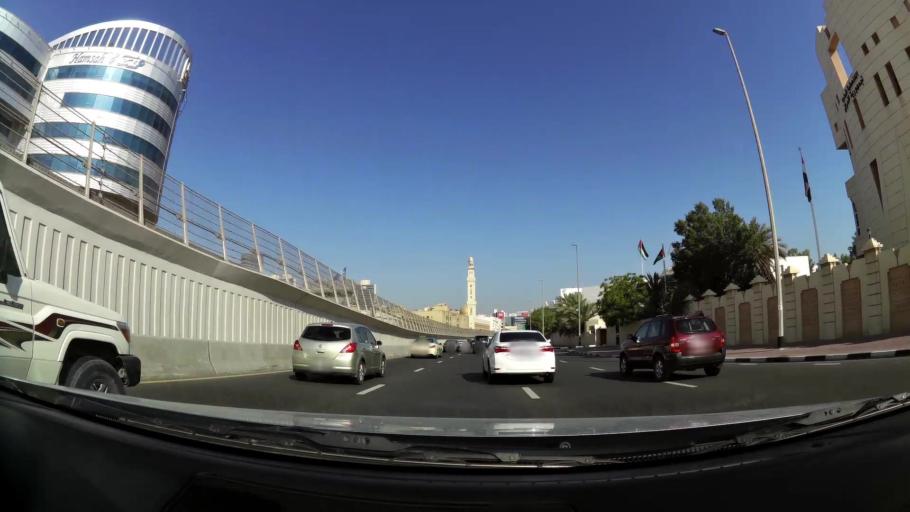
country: AE
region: Ash Shariqah
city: Sharjah
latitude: 25.2528
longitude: 55.3088
